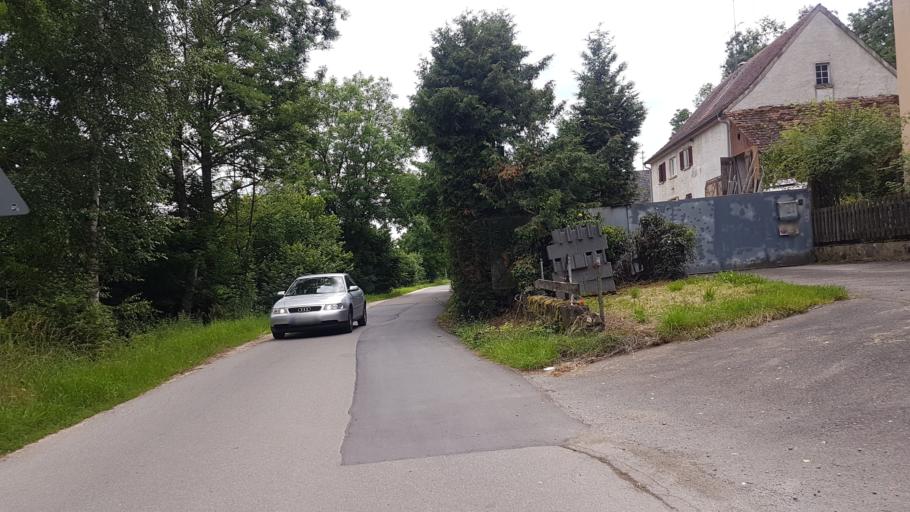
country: DE
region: Baden-Wuerttemberg
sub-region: Tuebingen Region
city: Scheer
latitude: 48.0680
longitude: 9.2956
